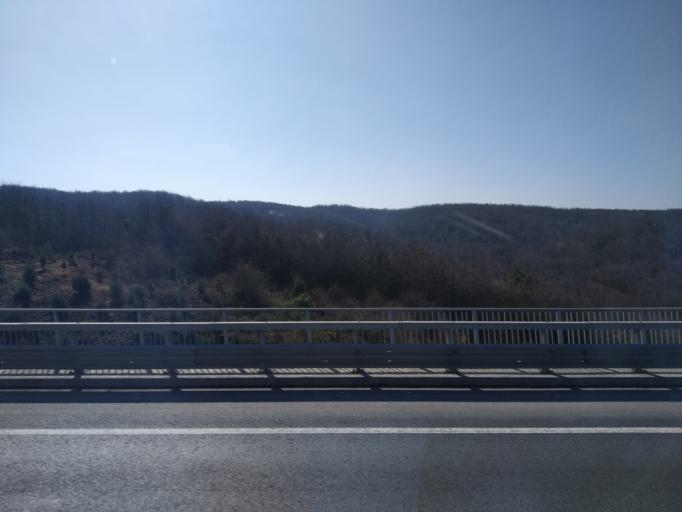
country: TR
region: Istanbul
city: Mahmut Sevket Pasa
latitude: 41.1690
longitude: 29.2503
